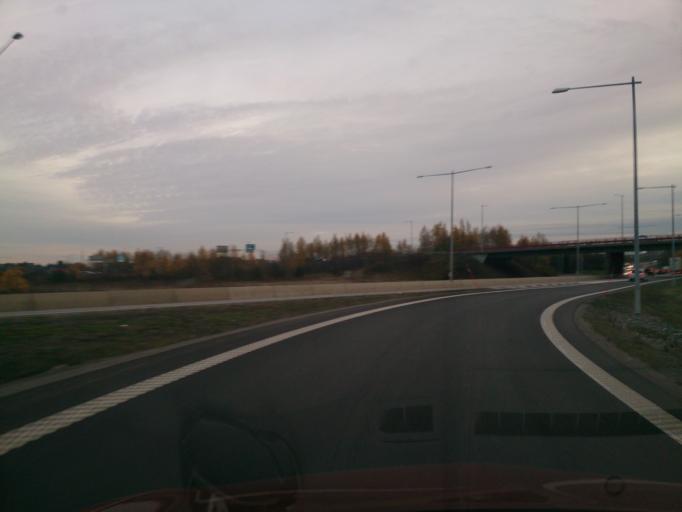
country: SE
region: OEstergoetland
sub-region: Norrkopings Kommun
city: Norrkoping
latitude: 58.6288
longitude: 16.1519
